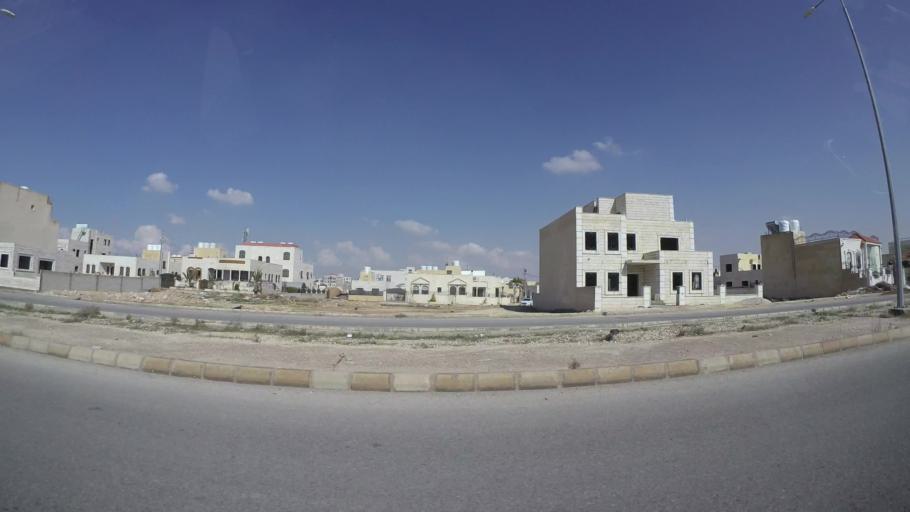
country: JO
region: Zarqa
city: Zarqa
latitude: 32.0588
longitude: 36.1135
